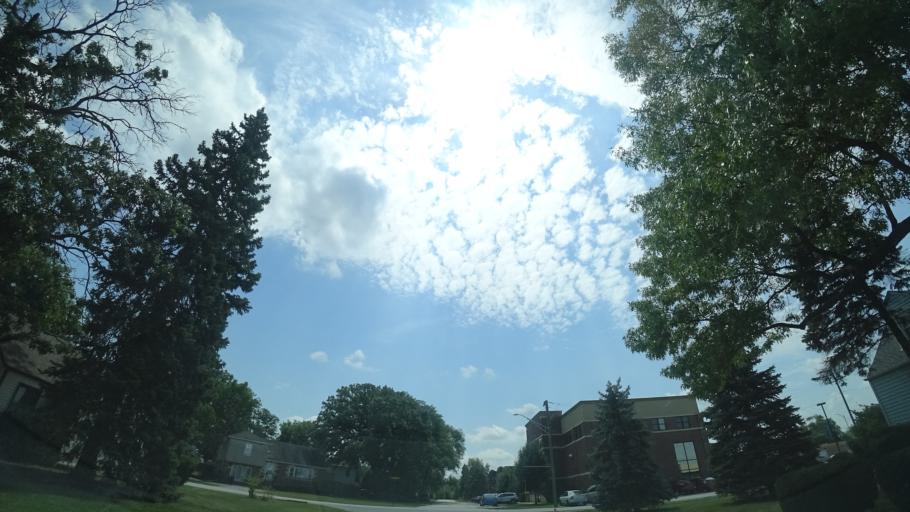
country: US
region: Illinois
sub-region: Cook County
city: Worth
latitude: 41.6880
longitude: -87.7963
